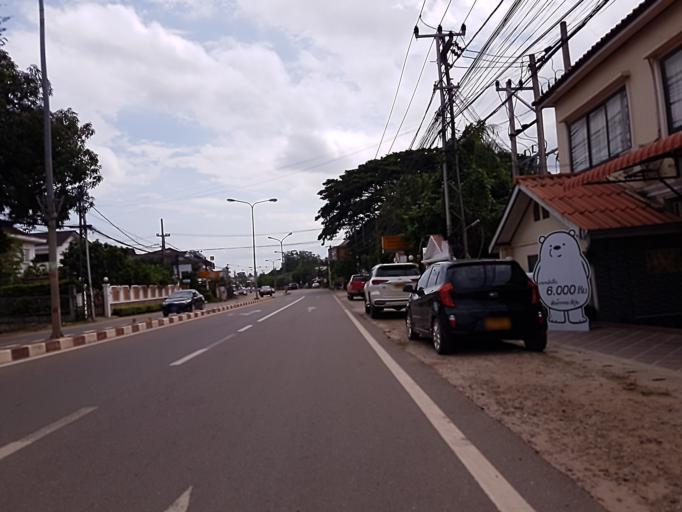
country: LA
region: Vientiane
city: Vientiane
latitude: 17.9325
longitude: 102.6164
